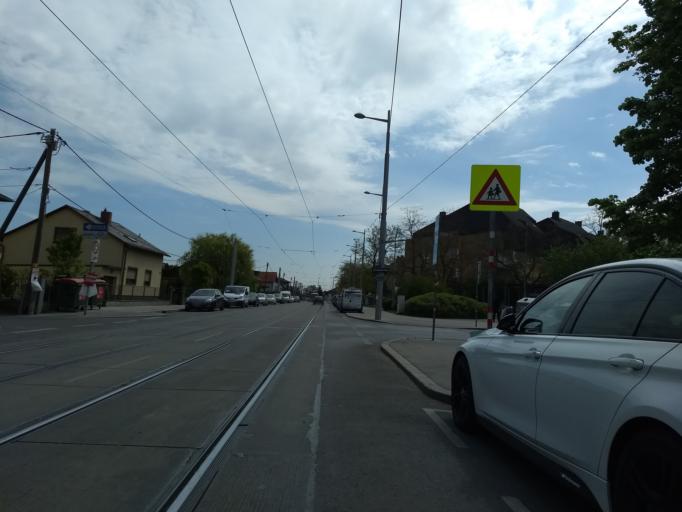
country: AT
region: Lower Austria
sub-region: Politischer Bezirk Wien-Umgebung
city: Gerasdorf bei Wien
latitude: 48.2379
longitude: 16.4856
